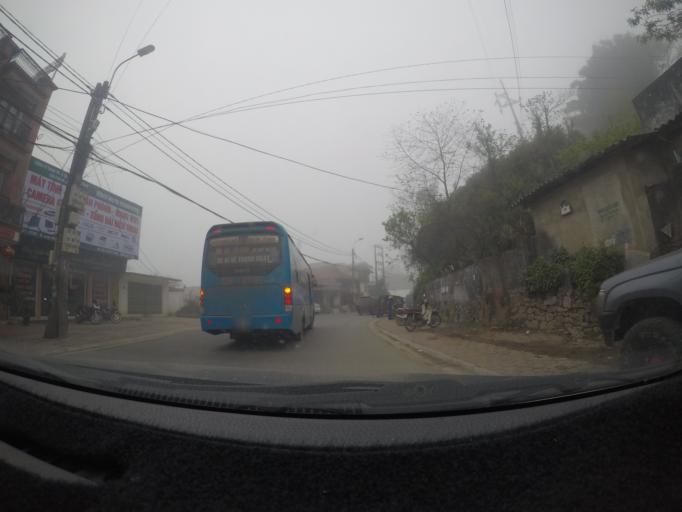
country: VN
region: Lao Cai
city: Sa Pa
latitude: 22.3417
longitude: 103.8555
